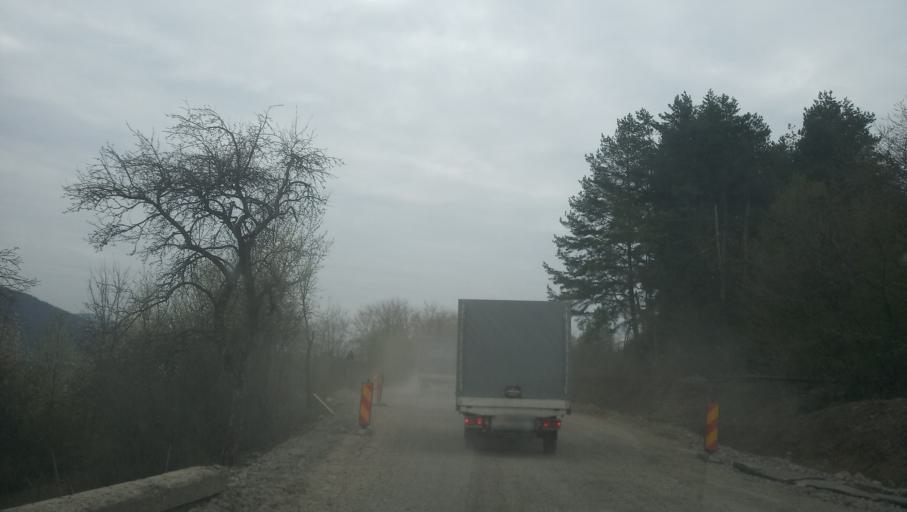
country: RO
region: Arad
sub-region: Comuna Varfurile
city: Varfurile
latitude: 46.3666
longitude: 22.5495
